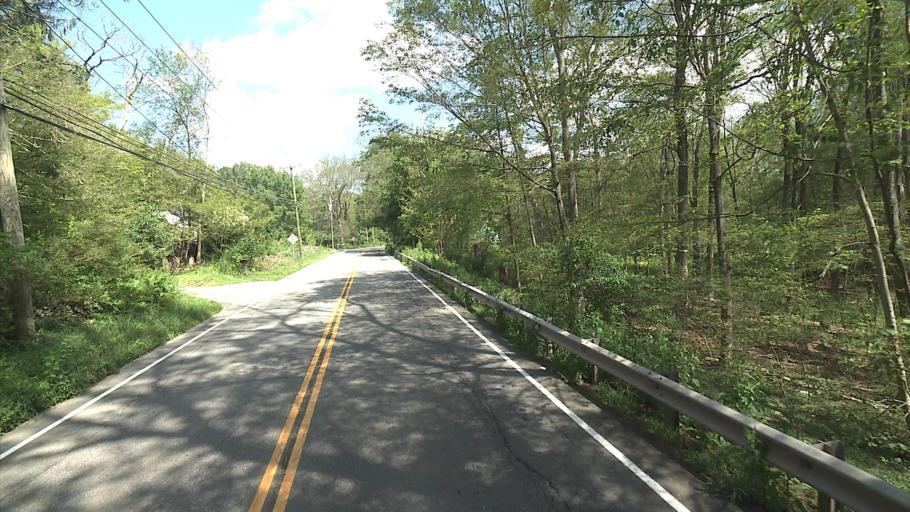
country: US
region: Connecticut
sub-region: Windham County
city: Windham
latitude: 41.7836
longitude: -72.1290
